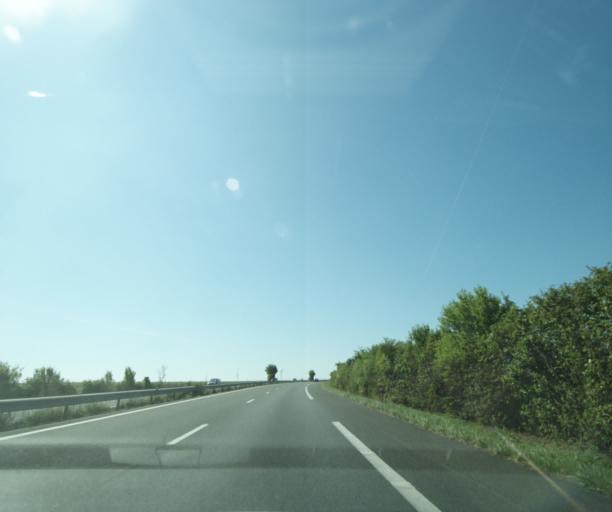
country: FR
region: Centre
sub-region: Departement de l'Indre
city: Vatan
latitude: 47.0601
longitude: 1.8192
